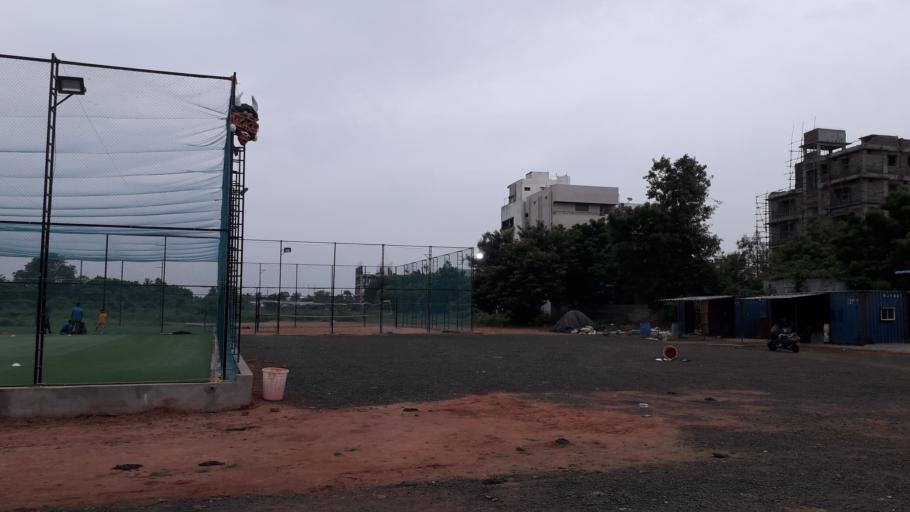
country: IN
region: Andhra Pradesh
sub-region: East Godavari
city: Rajahmundry
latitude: 17.0214
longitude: 81.8095
